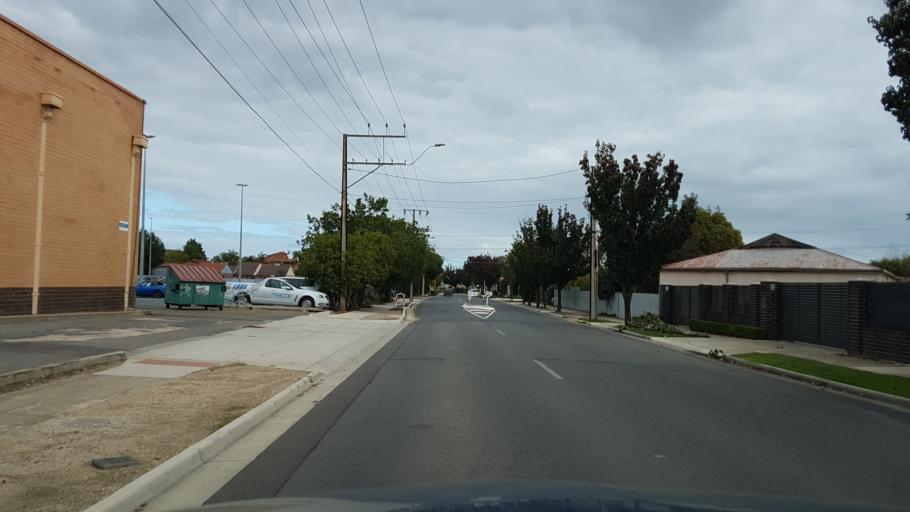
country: AU
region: South Australia
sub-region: Unley
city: Forestville
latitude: -34.9558
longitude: 138.5648
